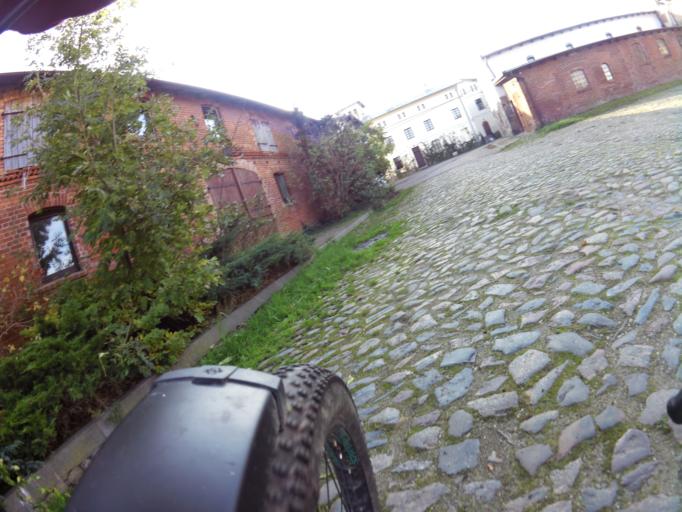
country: PL
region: Pomeranian Voivodeship
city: Strzelno
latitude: 54.7645
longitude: 18.2450
